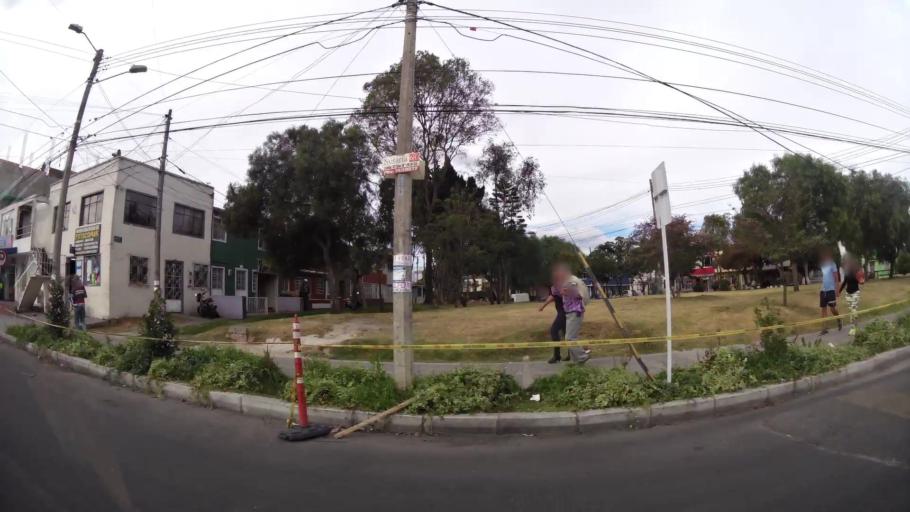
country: CO
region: Cundinamarca
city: Soacha
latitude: 4.6197
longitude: -74.1589
